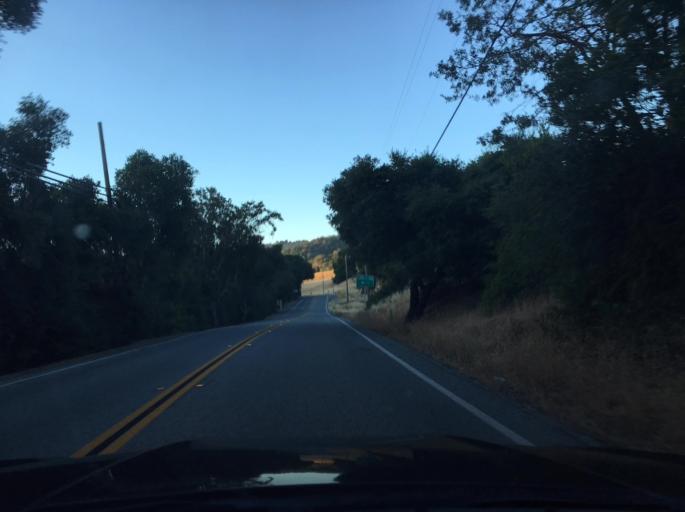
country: US
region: California
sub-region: Santa Clara County
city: Seven Trees
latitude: 37.1898
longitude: -121.7979
